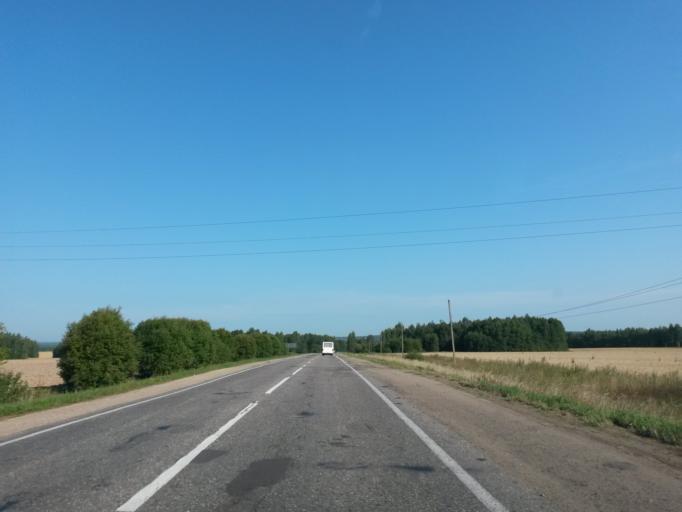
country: RU
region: Jaroslavl
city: Gavrilov-Yam
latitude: 57.3112
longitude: 39.9361
